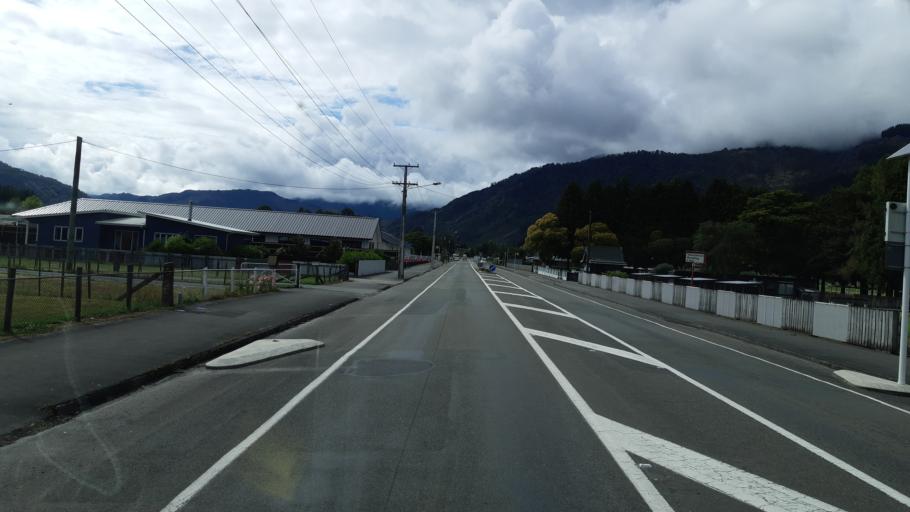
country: NZ
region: West Coast
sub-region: Buller District
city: Westport
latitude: -41.8000
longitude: 172.3300
